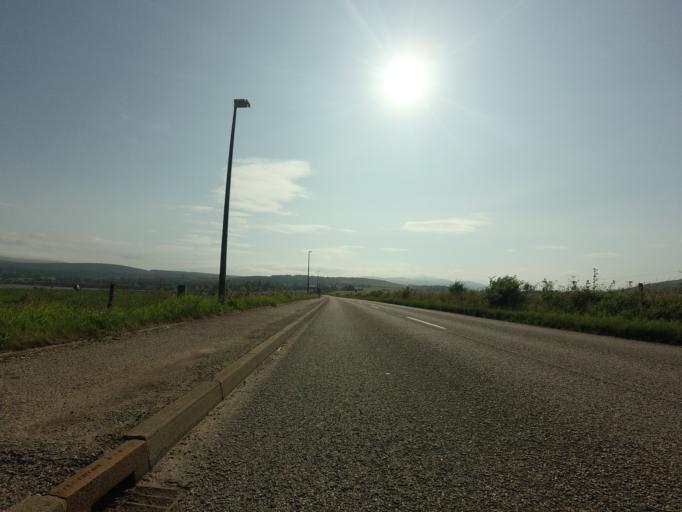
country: GB
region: Scotland
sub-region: Highland
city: Alness
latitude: 57.8882
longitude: -4.3560
